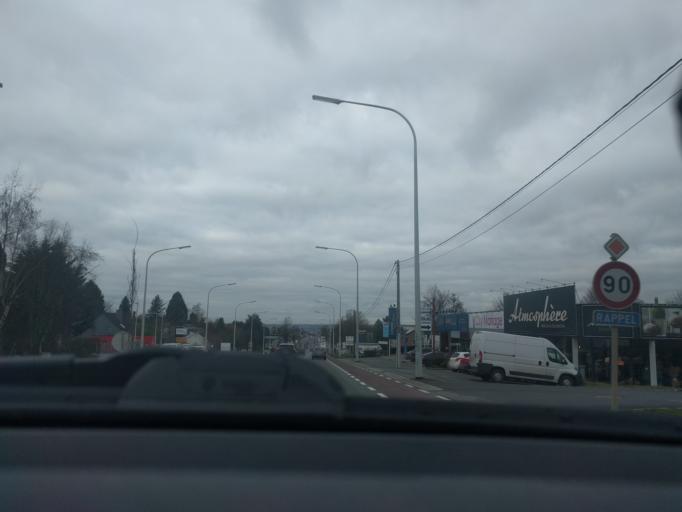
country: BE
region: Wallonia
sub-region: Province de Namur
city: Namur
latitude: 50.4362
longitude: 4.9137
